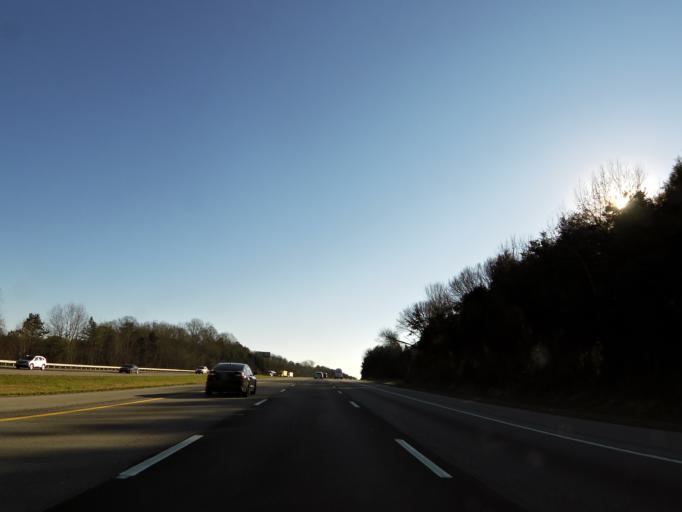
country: US
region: Tennessee
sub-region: Knox County
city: Mascot
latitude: 36.0038
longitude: -83.7426
